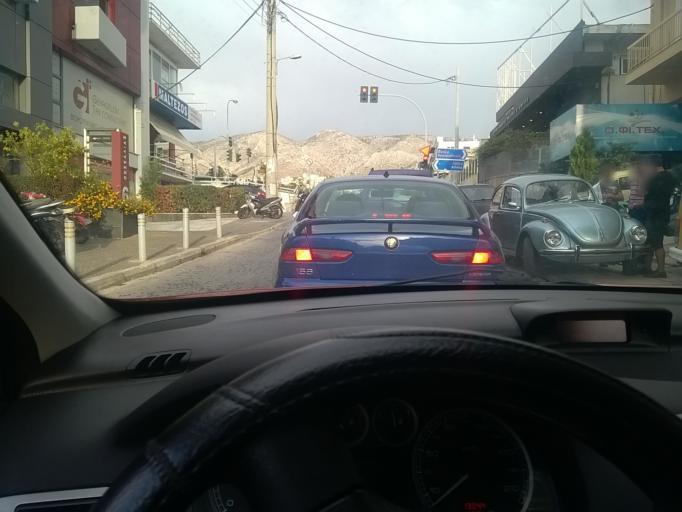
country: GR
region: Attica
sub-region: Nomarchia Athinas
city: Argyroupoli
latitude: 37.9200
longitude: 23.7436
